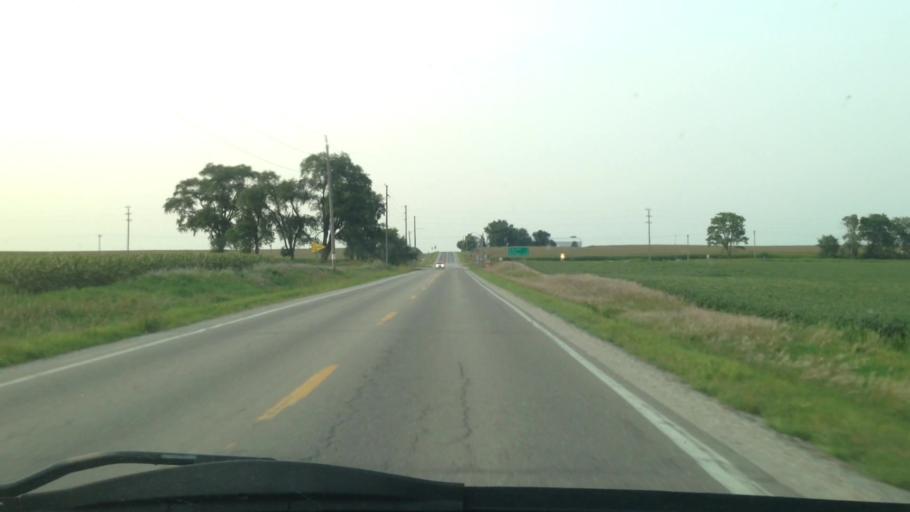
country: US
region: Iowa
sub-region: Iowa County
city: Marengo
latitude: 41.9613
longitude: -92.0853
